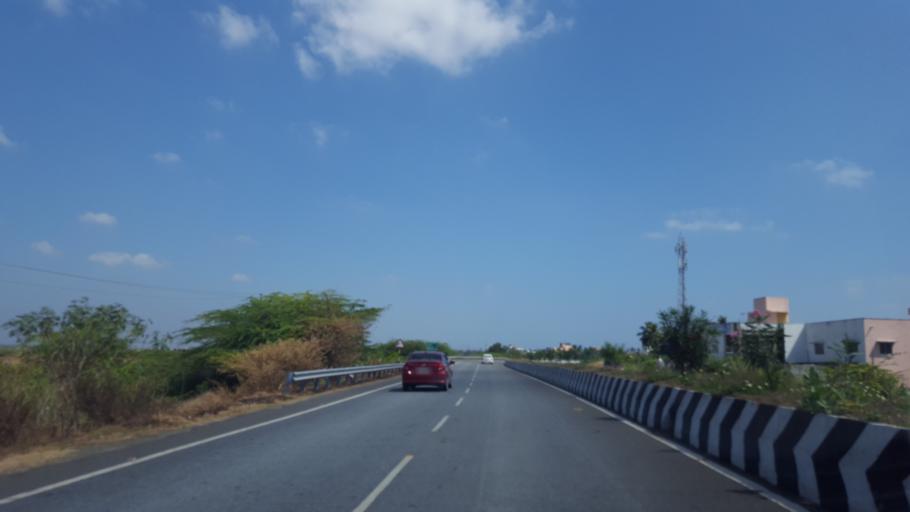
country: IN
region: Tamil Nadu
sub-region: Kancheepuram
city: Mamallapuram
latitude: 12.6249
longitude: 80.1915
